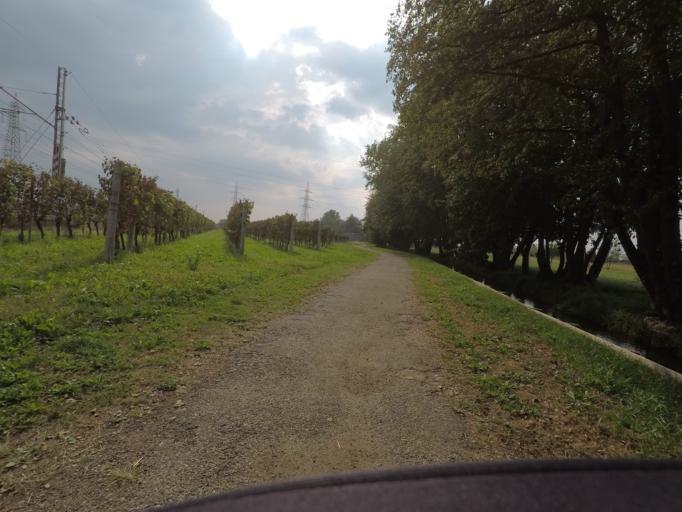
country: IT
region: Friuli Venezia Giulia
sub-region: Provincia di Udine
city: Reana del Rojale
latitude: 46.1216
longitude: 13.2453
